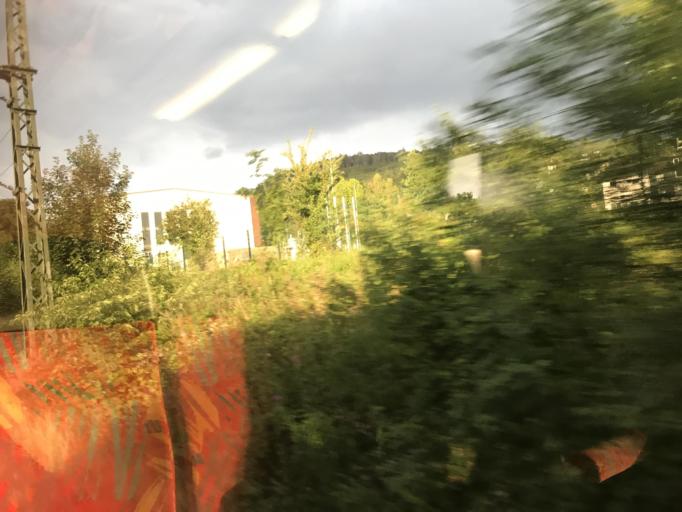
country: DE
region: Rheinland-Pfalz
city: Mudersbach
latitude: 50.8336
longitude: 7.9565
